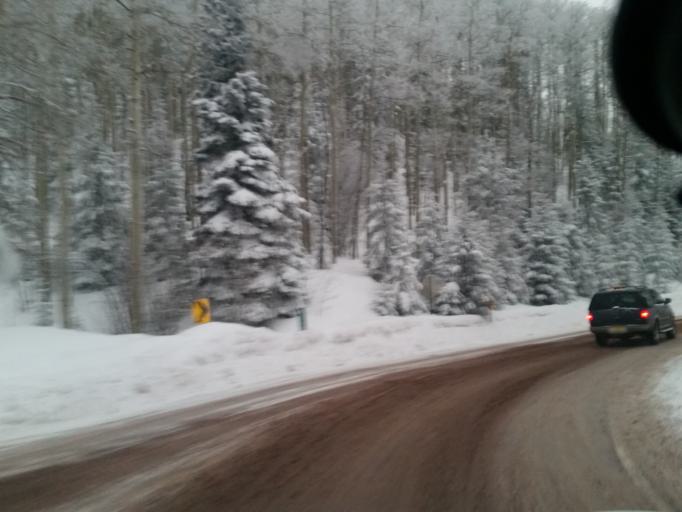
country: US
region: New Mexico
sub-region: Santa Fe County
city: Santa Fe
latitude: 35.7693
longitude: -105.8093
